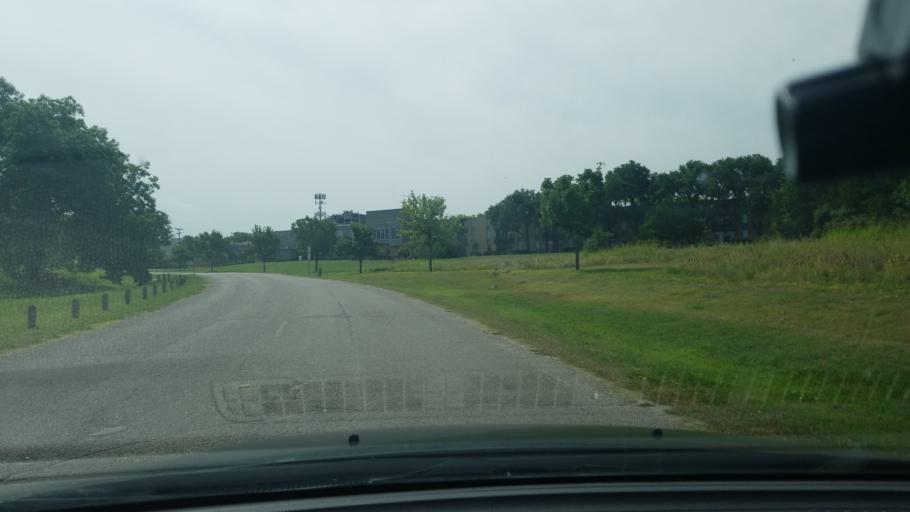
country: US
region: Texas
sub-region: Dallas County
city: Highland Park
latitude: 32.8303
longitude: -96.7124
